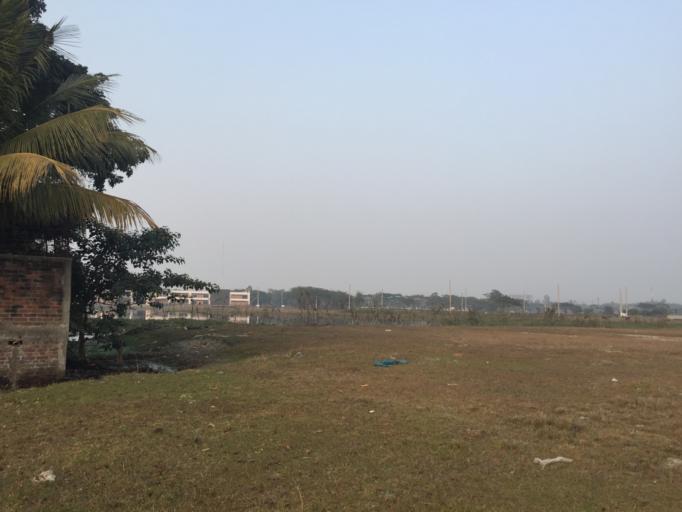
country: BD
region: Dhaka
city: Tungi
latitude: 23.8674
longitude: 90.3121
